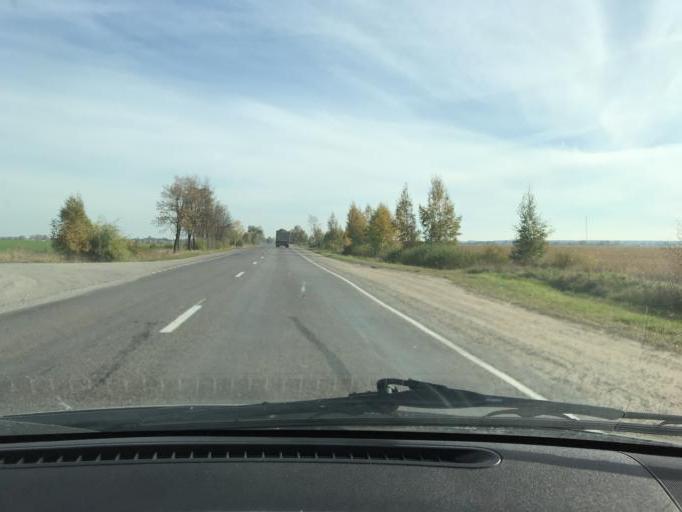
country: BY
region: Brest
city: Asnyezhytsy
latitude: 52.2132
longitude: 26.0439
